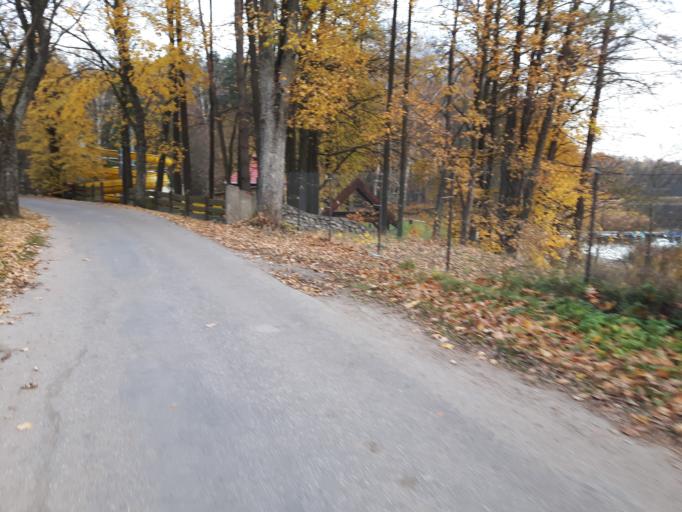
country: PL
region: Warmian-Masurian Voivodeship
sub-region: Powiat olsztynski
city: Barczewo
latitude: 53.8296
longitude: 20.7366
